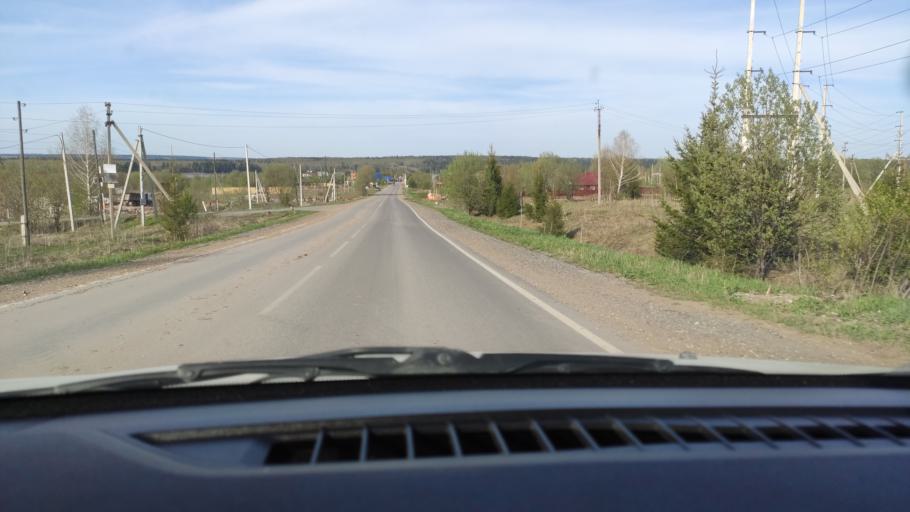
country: RU
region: Perm
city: Sylva
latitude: 57.9281
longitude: 56.6868
